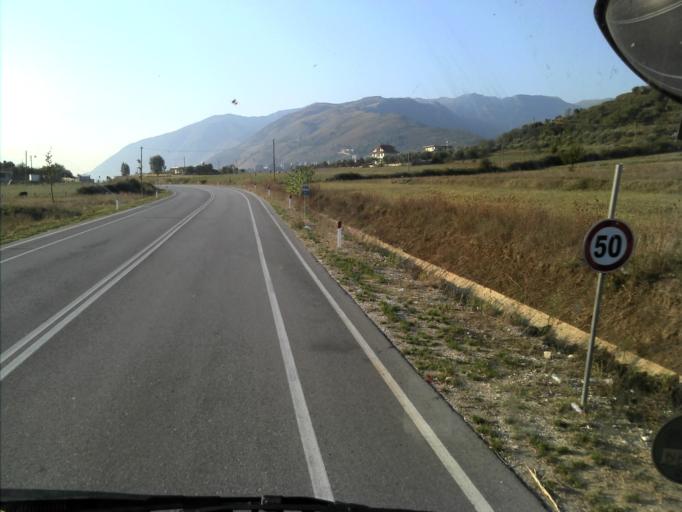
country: AL
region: Gjirokaster
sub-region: Rrethi i Tepelenes
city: Tepelene
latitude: 40.3125
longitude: 20.0143
